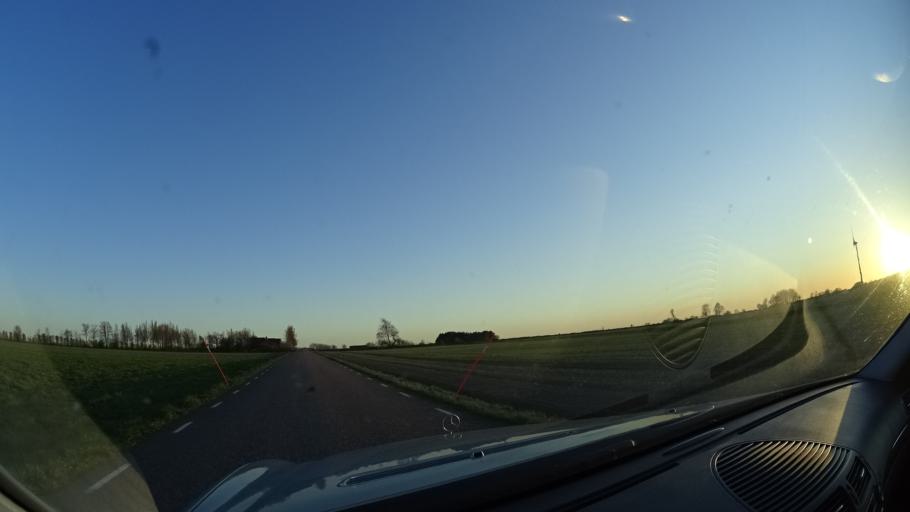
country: SE
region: Skane
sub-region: Hoors Kommun
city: Loberod
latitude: 55.8268
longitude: 13.4504
